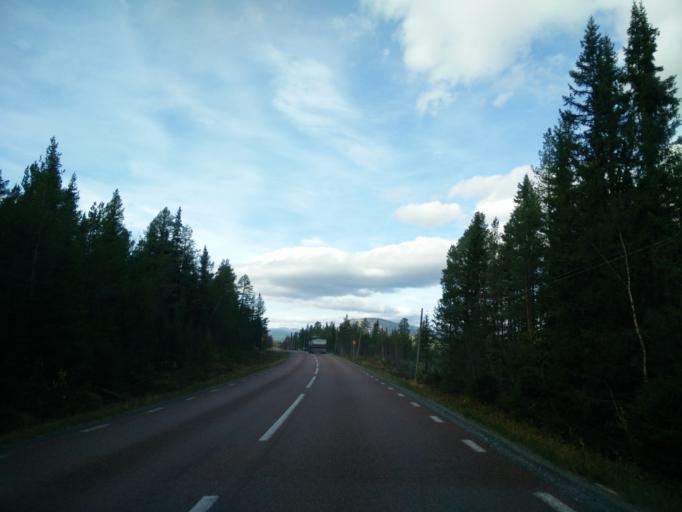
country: NO
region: Hedmark
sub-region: Engerdal
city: Engerdal
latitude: 62.5023
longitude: 12.6248
